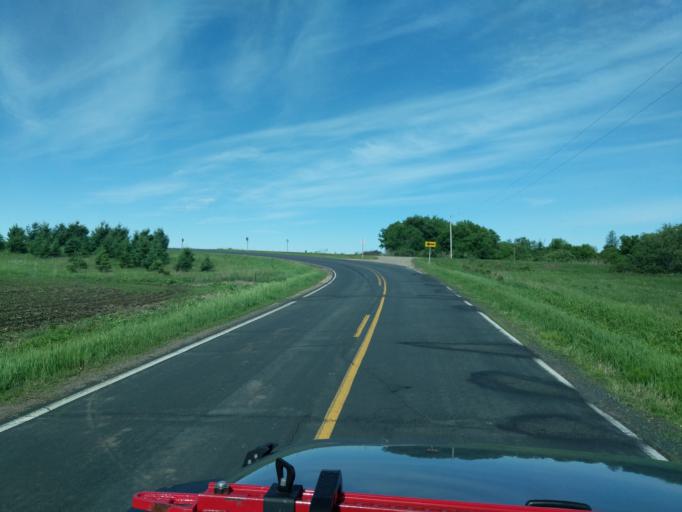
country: US
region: Wisconsin
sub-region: Saint Croix County
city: Hammond
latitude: 44.8806
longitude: -92.4955
